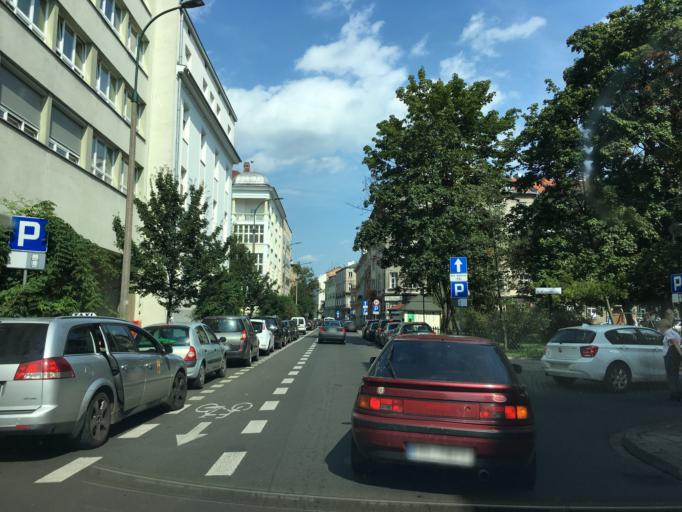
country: PL
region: Lesser Poland Voivodeship
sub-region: Krakow
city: Krakow
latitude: 50.0609
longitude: 19.9275
